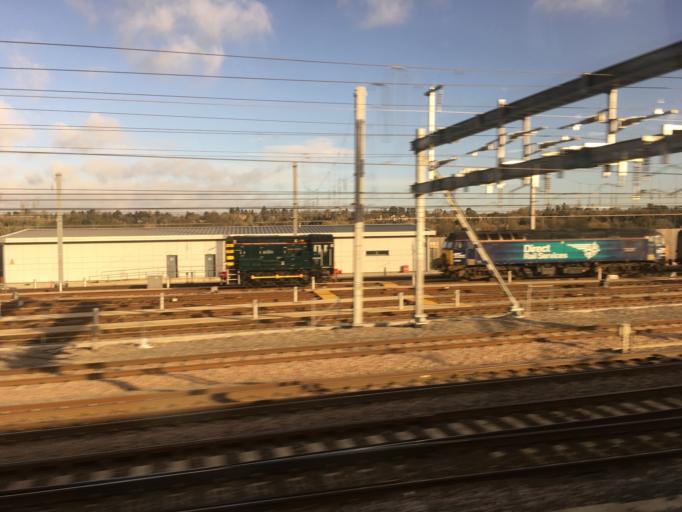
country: GB
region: England
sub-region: Reading
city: Reading
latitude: 51.4626
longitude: -1.0022
